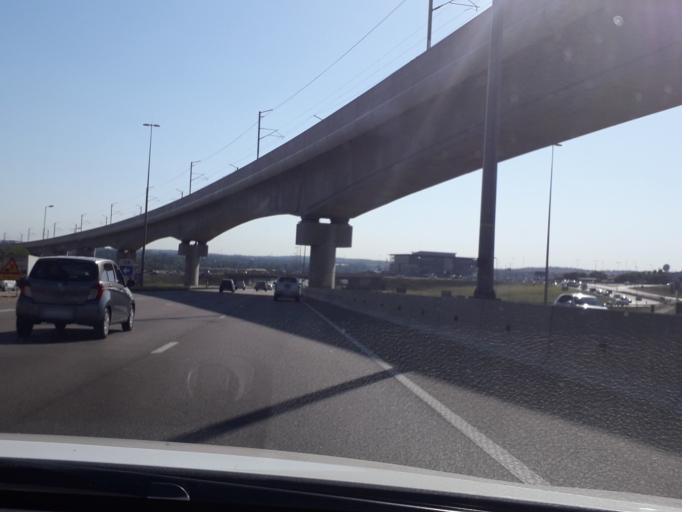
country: ZA
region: Gauteng
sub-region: City of Tshwane Metropolitan Municipality
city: Centurion
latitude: -25.8687
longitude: 28.1890
